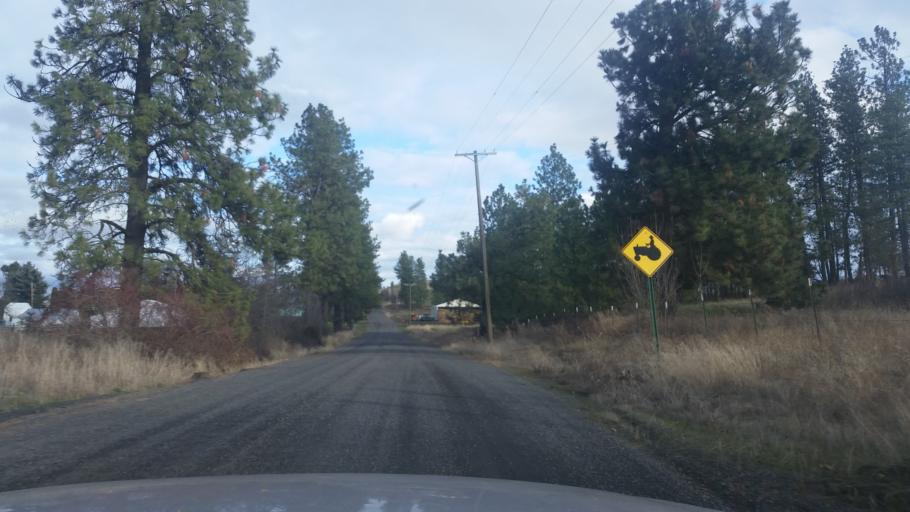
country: US
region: Washington
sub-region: Spokane County
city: Cheney
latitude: 47.4272
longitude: -117.4337
